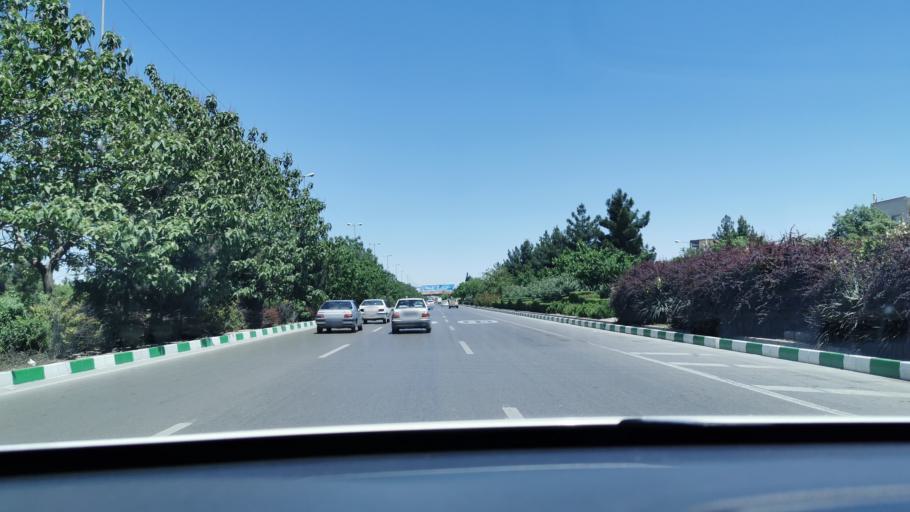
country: IR
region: Razavi Khorasan
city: Mashhad
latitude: 36.2581
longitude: 59.6274
